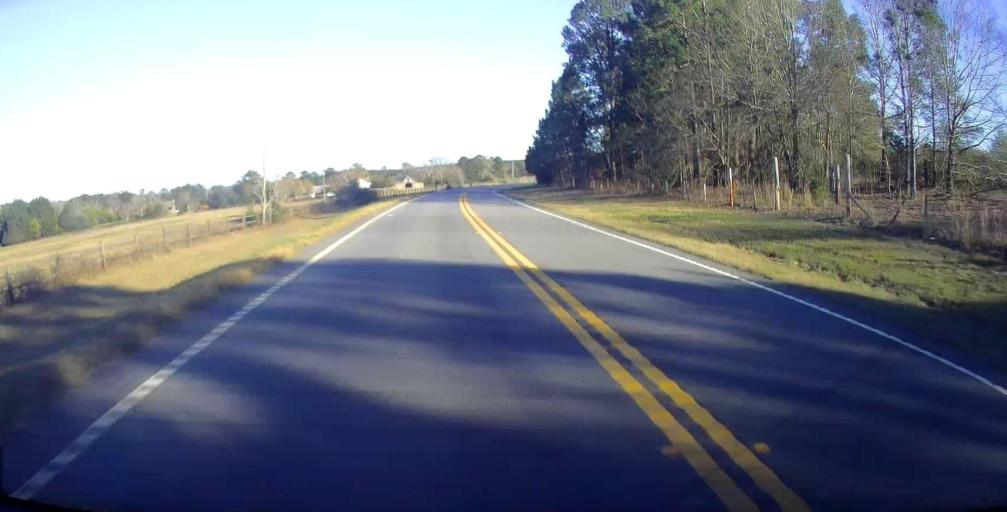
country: US
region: Georgia
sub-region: Taylor County
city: Butler
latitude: 32.4721
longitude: -84.3665
